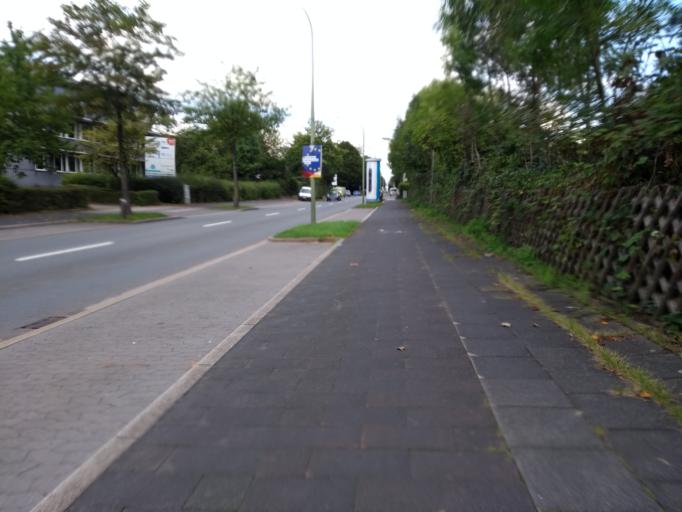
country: DE
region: North Rhine-Westphalia
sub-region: Regierungsbezirk Arnsberg
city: Hagen
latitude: 51.3894
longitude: 7.4639
